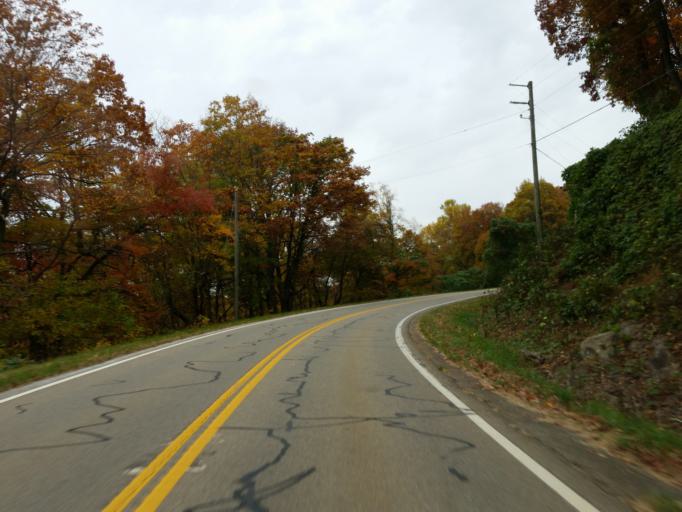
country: US
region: Georgia
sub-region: Pickens County
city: Jasper
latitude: 34.5402
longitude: -84.3712
